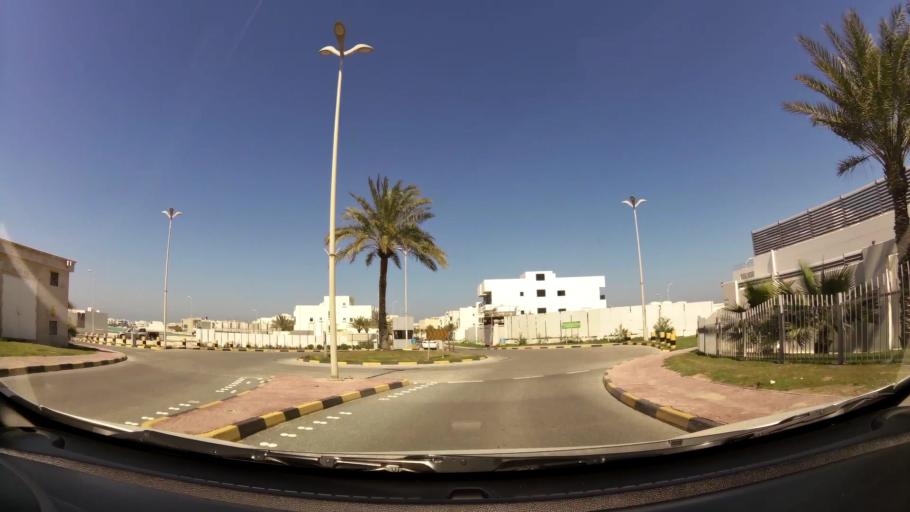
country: BH
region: Muharraq
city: Al Hadd
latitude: 26.2876
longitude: 50.6733
